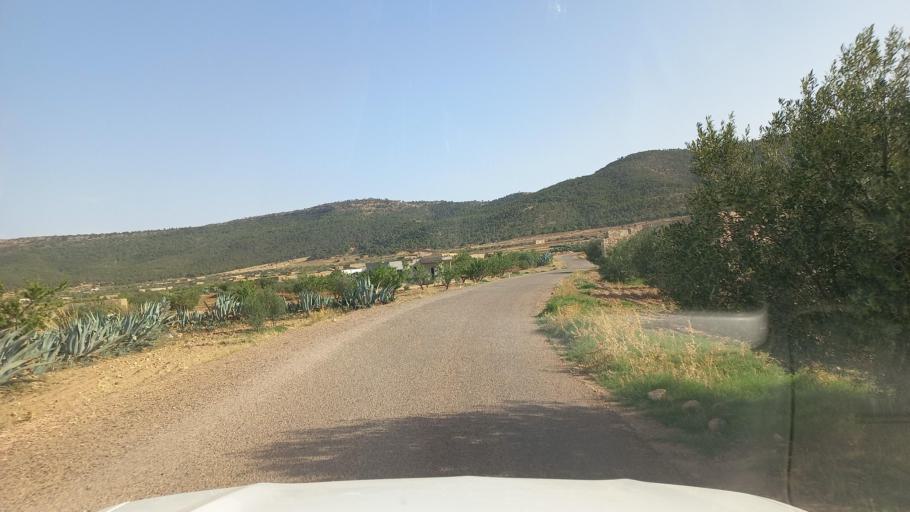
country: TN
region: Al Qasrayn
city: Kasserine
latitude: 35.3440
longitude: 8.8344
